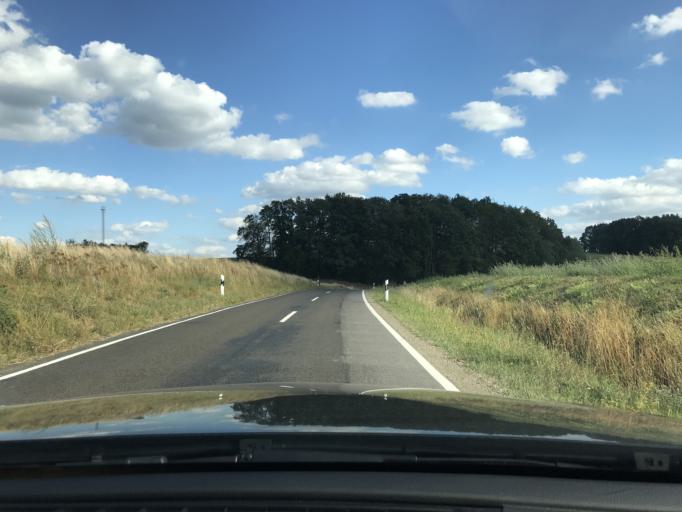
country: DE
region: Bavaria
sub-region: Regierungsbezirk Unterfranken
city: Kirchlauter
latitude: 50.0759
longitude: 10.6619
